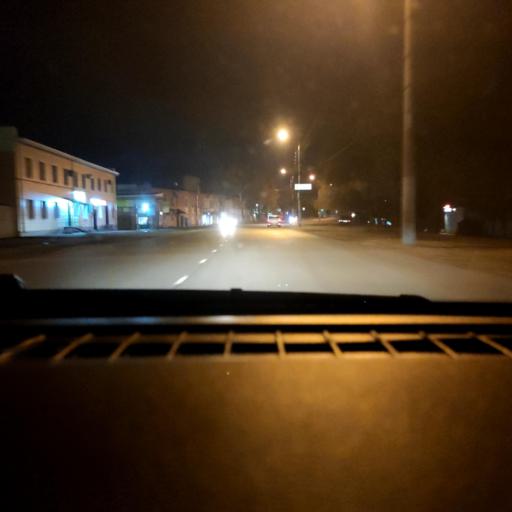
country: RU
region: Voronezj
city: Voronezh
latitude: 51.6267
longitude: 39.1763
